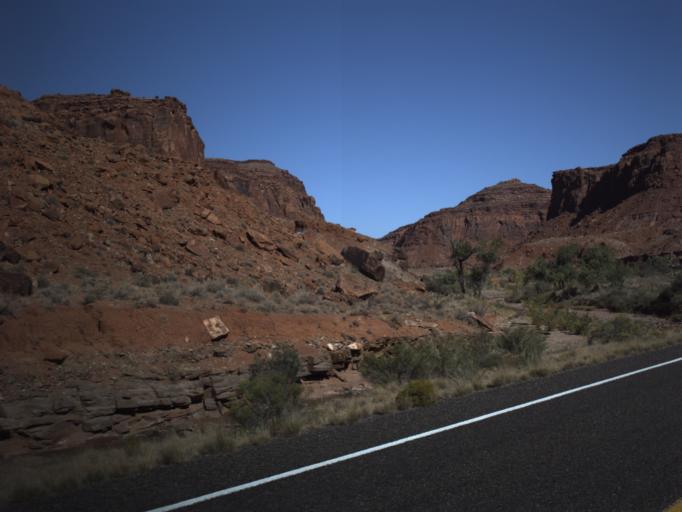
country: US
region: Utah
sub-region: San Juan County
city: Blanding
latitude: 37.9264
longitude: -110.4647
